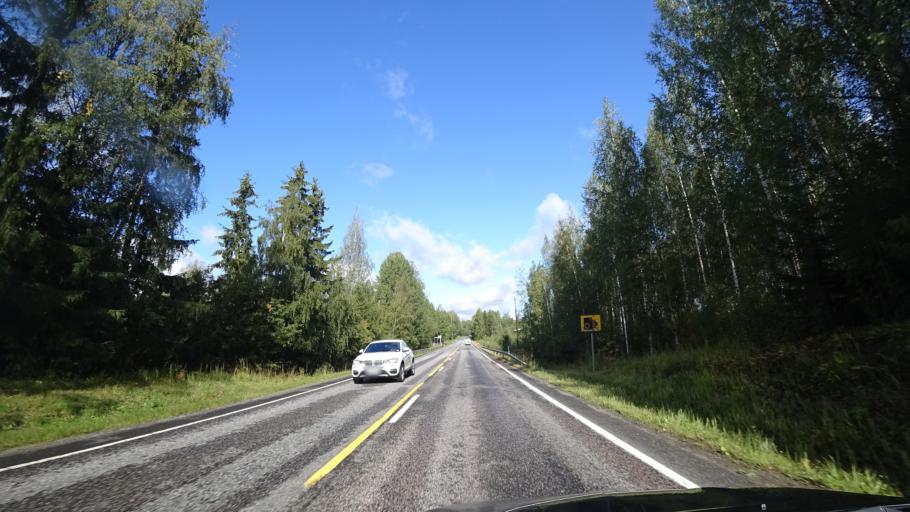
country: FI
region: Uusimaa
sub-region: Helsinki
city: Tuusula
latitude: 60.4444
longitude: 24.9710
